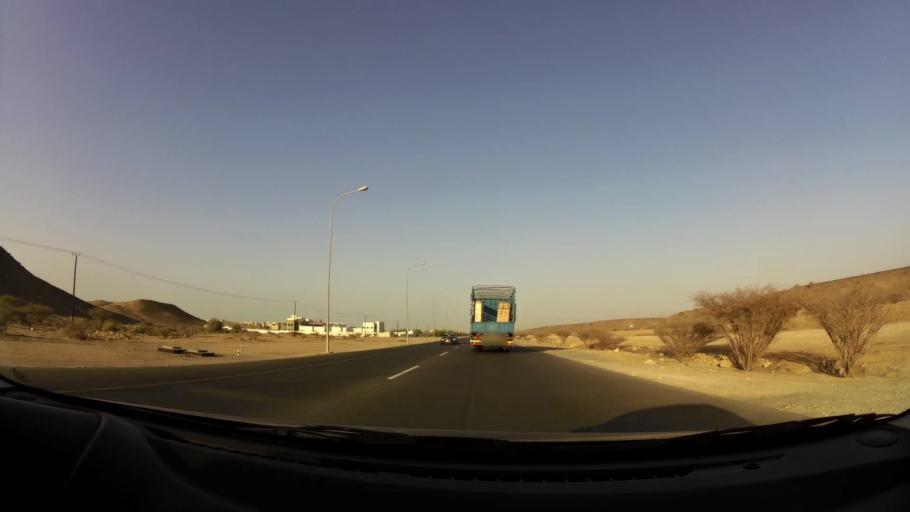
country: OM
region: Muhafazat Masqat
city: As Sib al Jadidah
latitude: 23.5813
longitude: 58.1574
